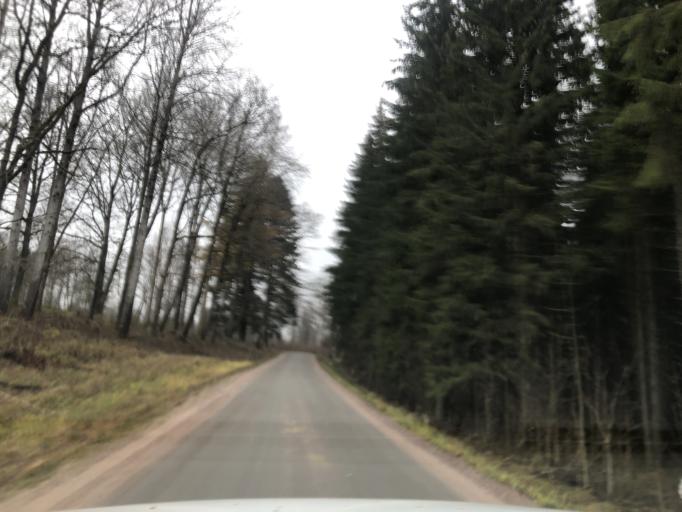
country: SE
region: Vaestra Goetaland
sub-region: Ulricehamns Kommun
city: Ulricehamn
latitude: 57.8471
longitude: 13.6361
